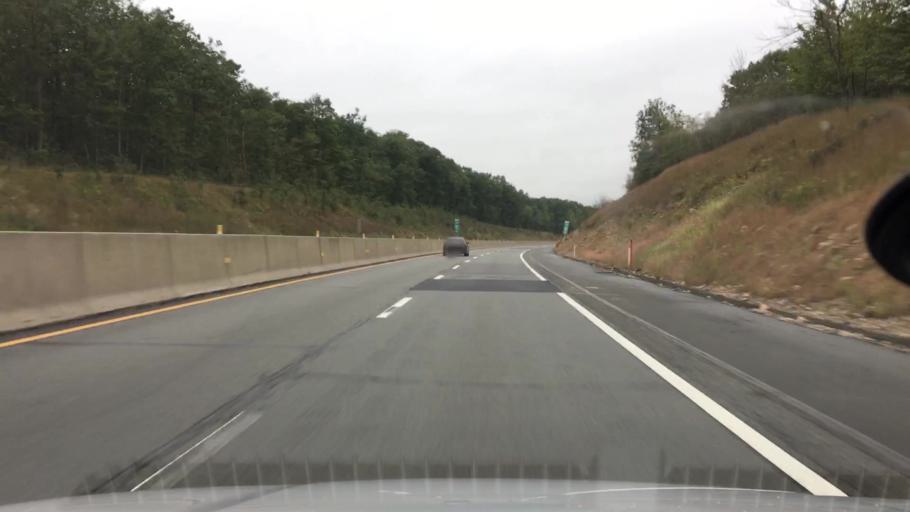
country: US
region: Pennsylvania
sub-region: Luzerne County
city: White Haven
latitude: 41.0785
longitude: -75.7289
